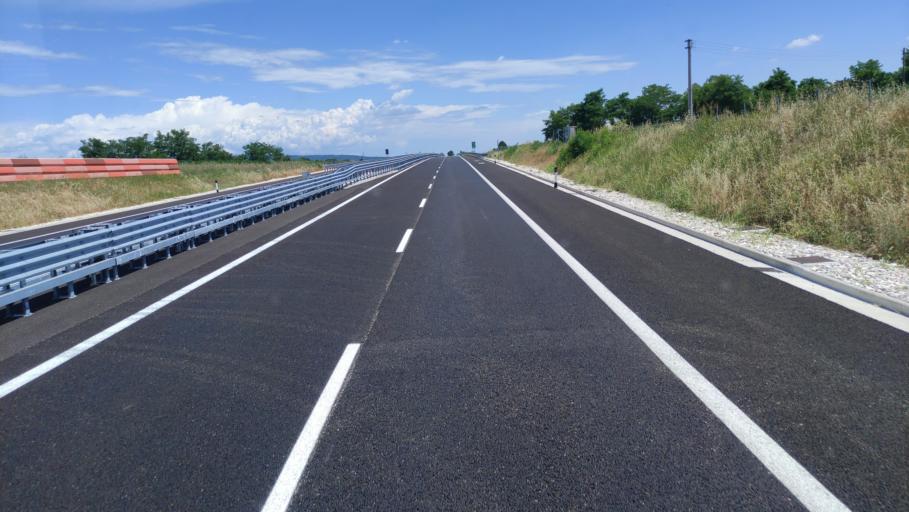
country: IT
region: Veneto
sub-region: Provincia di Treviso
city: Trevignano
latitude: 45.7344
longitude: 12.0362
